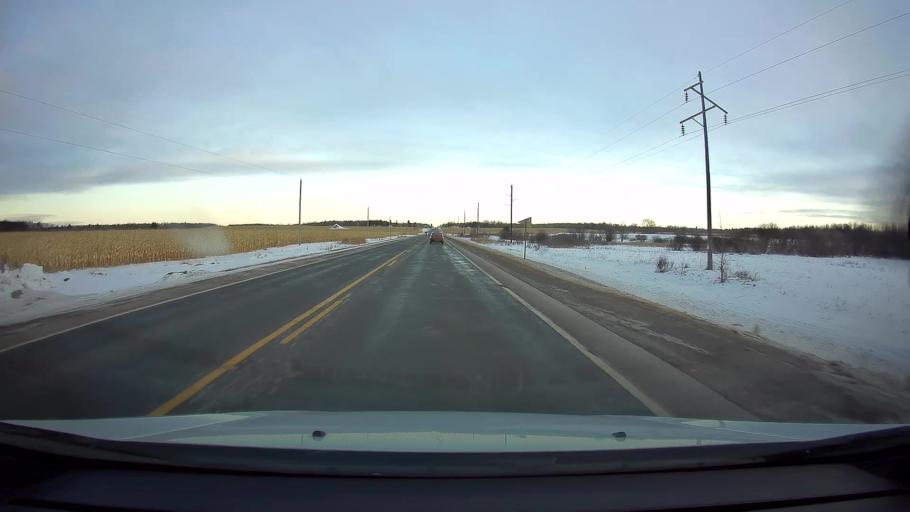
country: US
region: Wisconsin
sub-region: Barron County
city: Turtle Lake
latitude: 45.3433
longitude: -92.1668
